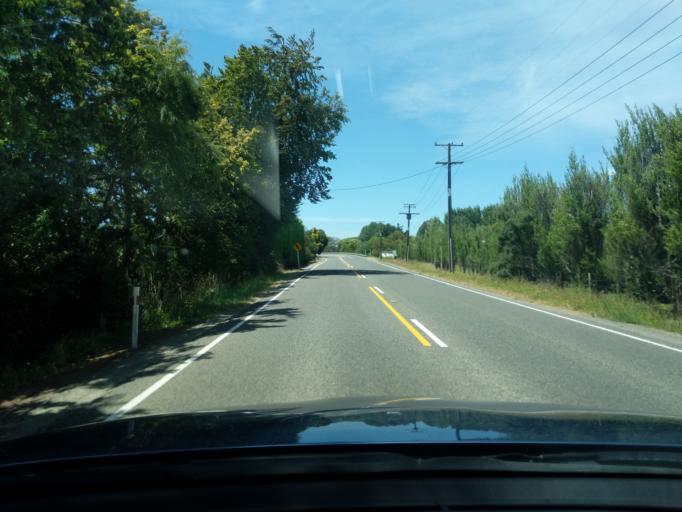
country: NZ
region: Tasman
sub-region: Tasman District
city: Motueka
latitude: -41.0909
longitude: 173.0024
